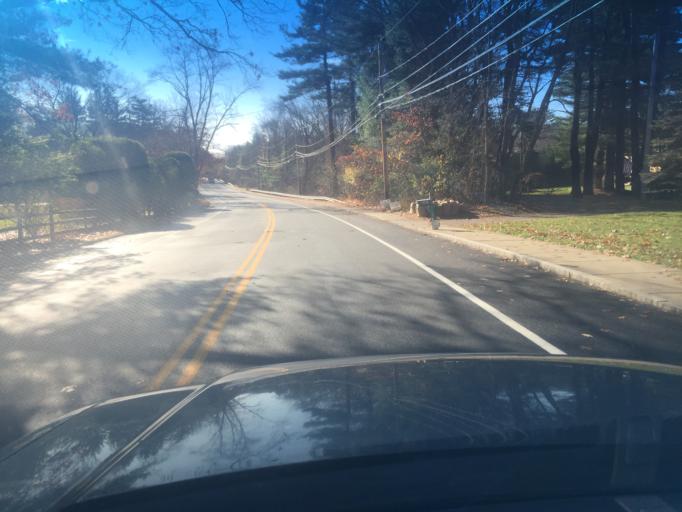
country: US
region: Massachusetts
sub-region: Norfolk County
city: Medway
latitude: 42.1306
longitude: -71.4323
